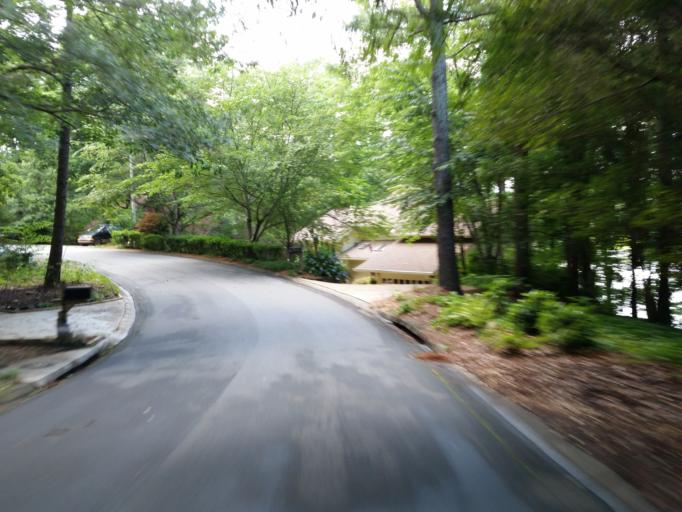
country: US
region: Georgia
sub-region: Fulton County
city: Roswell
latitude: 34.0419
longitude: -84.4244
